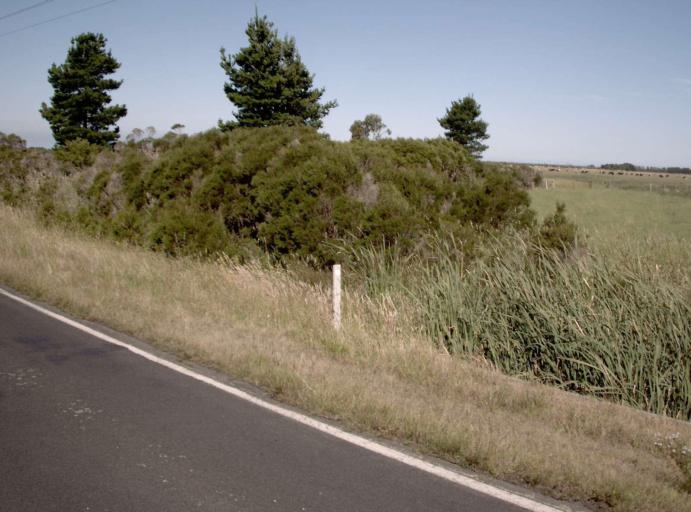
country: AU
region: Victoria
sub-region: Latrobe
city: Traralgon
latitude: -38.6292
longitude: 146.5973
